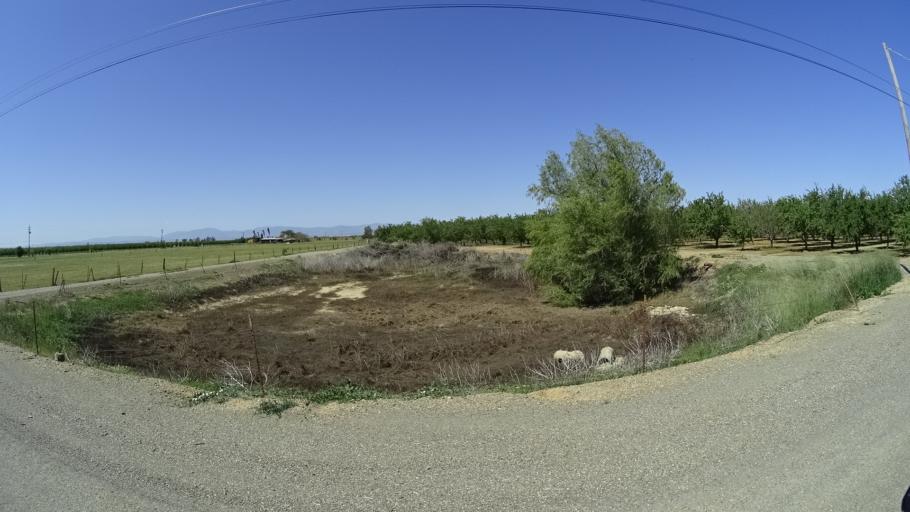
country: US
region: California
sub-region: Glenn County
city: Orland
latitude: 39.6980
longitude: -122.1639
